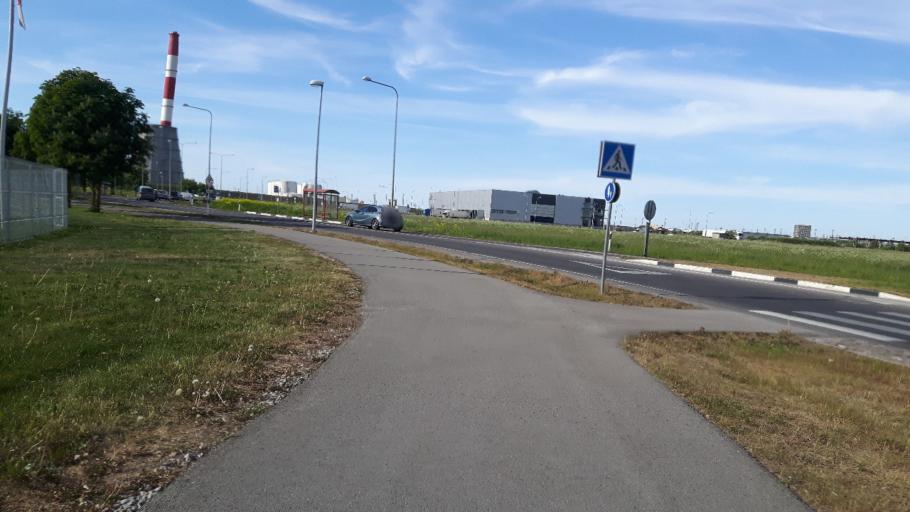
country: EE
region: Harju
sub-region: Joelaehtme vald
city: Loo
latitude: 59.4432
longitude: 24.9301
